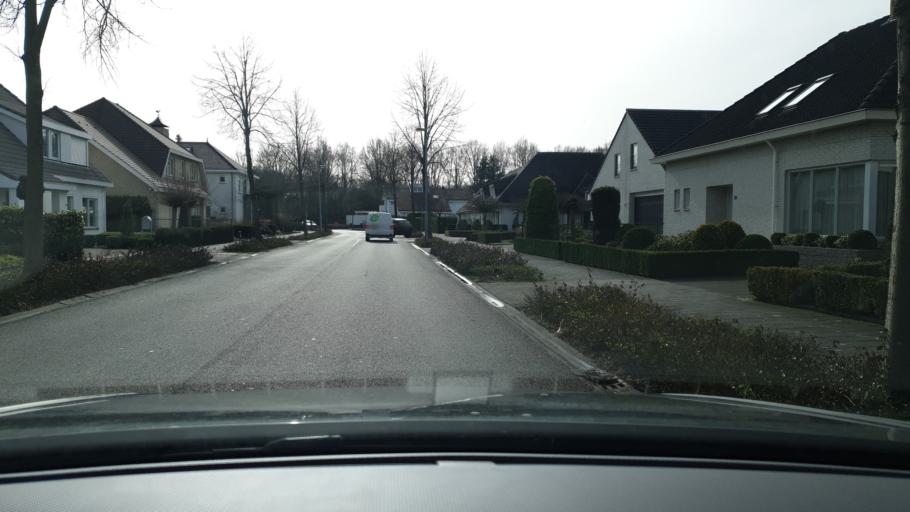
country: NL
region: North Brabant
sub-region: Gemeente Eindhoven
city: Meerhoven
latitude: 51.4728
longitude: 5.4332
